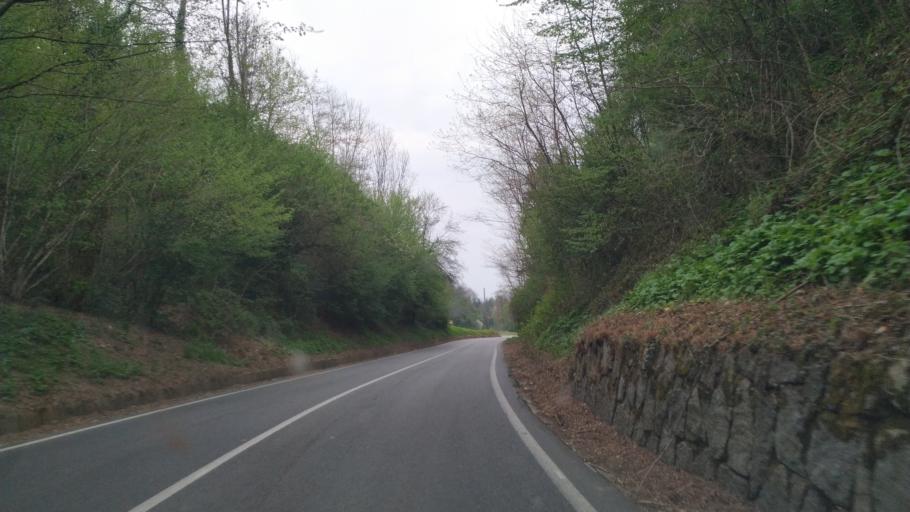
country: IT
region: Piedmont
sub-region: Provincia di Biella
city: Occhieppo Superiore
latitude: 45.5670
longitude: 8.0225
